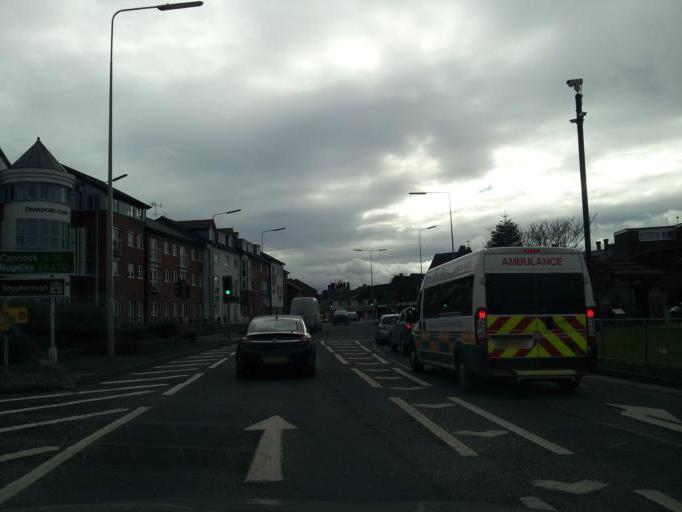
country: GB
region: England
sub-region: Staffordshire
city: Stafford
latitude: 52.8031
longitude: -2.1126
